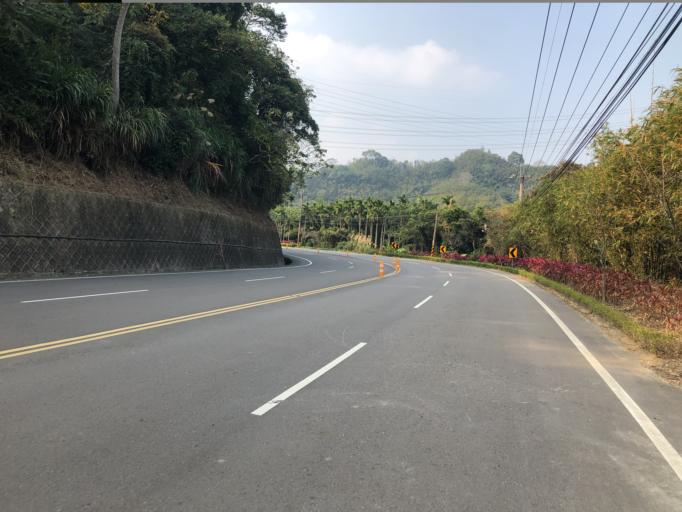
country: TW
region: Taiwan
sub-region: Miaoli
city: Miaoli
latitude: 24.6133
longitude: 120.9577
